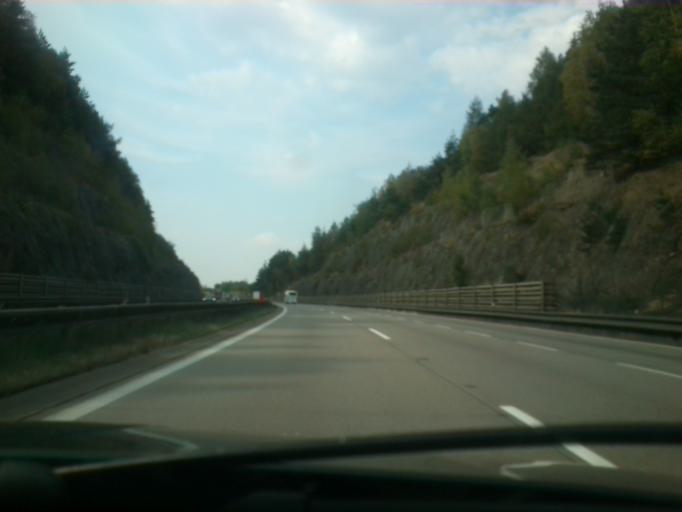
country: CZ
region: Central Bohemia
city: Ondrejov
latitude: 49.8859
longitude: 14.7560
